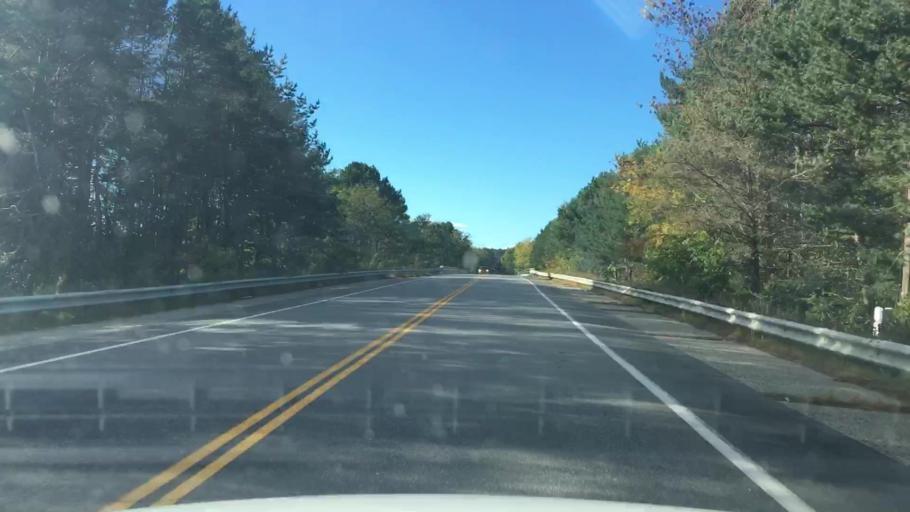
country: US
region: Maine
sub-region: Sagadahoc County
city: Topsham
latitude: 43.9271
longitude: -69.9982
